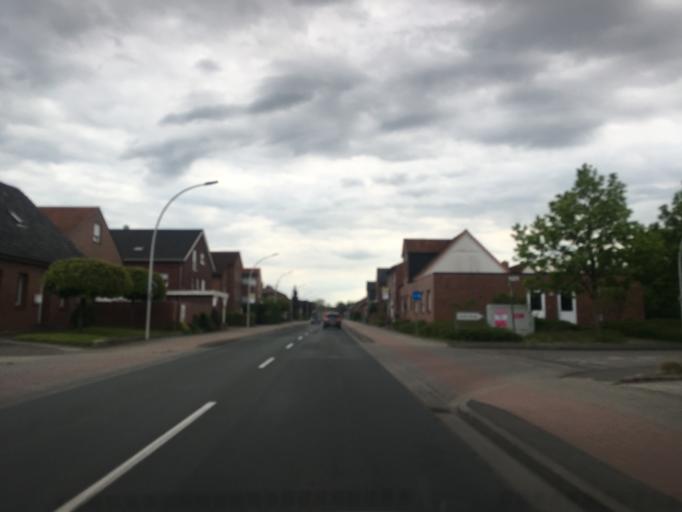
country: DE
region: North Rhine-Westphalia
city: Emsdetten
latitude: 52.1582
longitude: 7.5274
